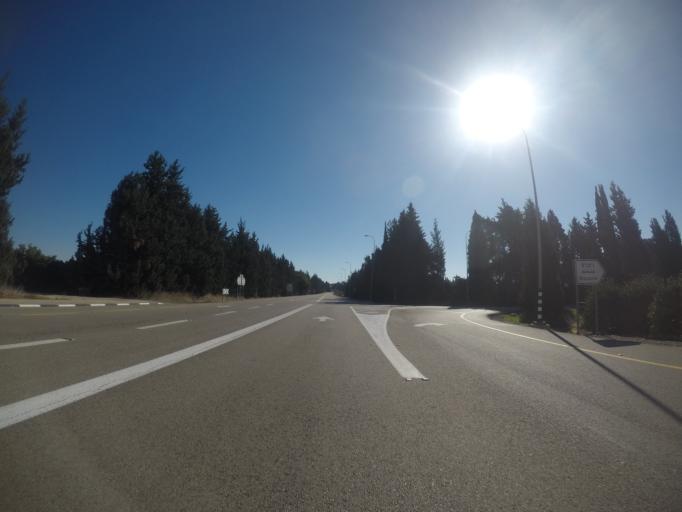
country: IL
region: Southern District
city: Ashdod
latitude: 31.7220
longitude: 34.6393
